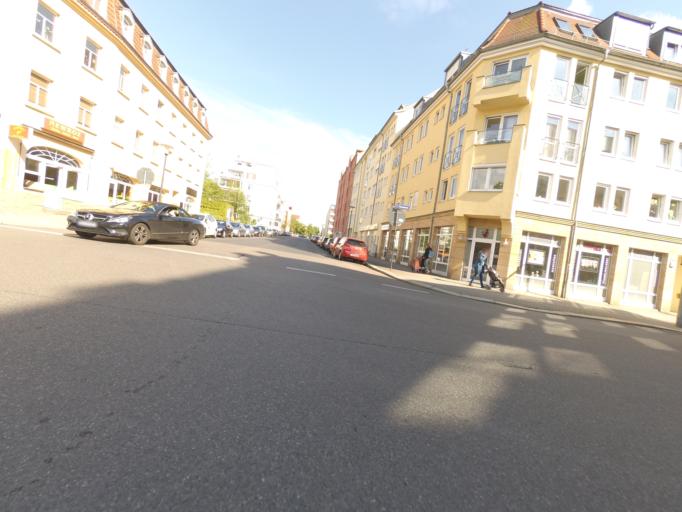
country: DE
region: Saxony
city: Albertstadt
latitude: 51.0477
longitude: 13.7823
